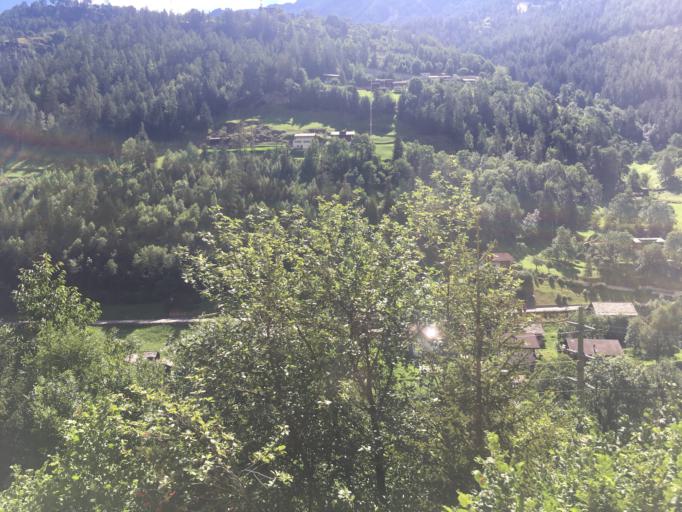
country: CH
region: Valais
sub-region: Visp District
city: Sankt Niklaus
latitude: 46.1879
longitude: 7.8089
